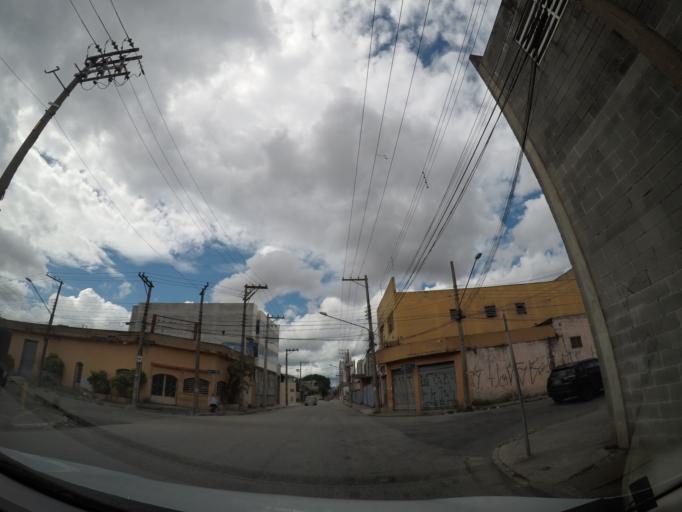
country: BR
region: Sao Paulo
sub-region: Guarulhos
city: Guarulhos
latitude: -23.4886
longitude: -46.5527
